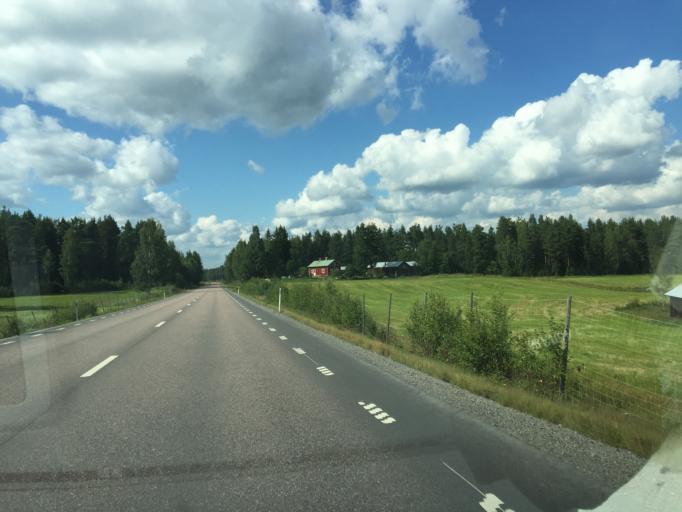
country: SE
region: Gaevleborg
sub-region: Bollnas Kommun
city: Bollnas
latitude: 61.3026
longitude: 16.4693
